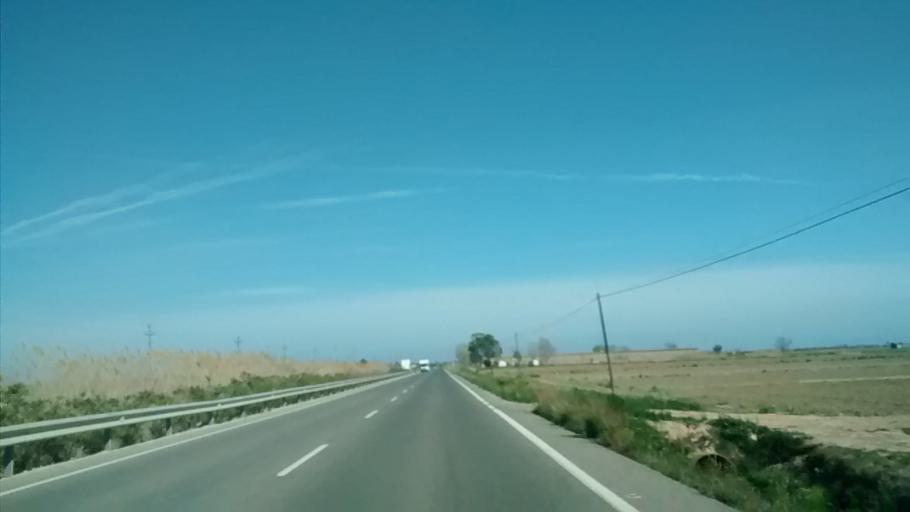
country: ES
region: Catalonia
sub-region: Provincia de Tarragona
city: Deltebre
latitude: 40.7053
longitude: 0.7815
